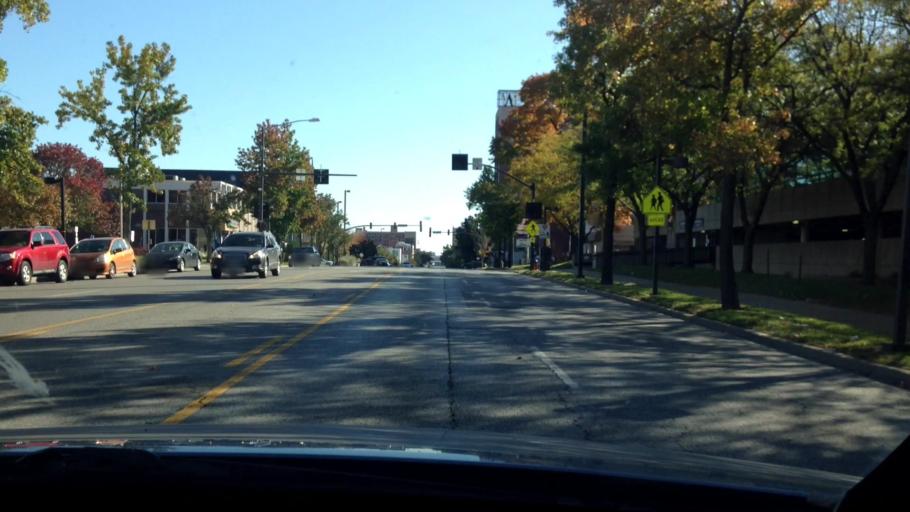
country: US
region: Missouri
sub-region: Jackson County
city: Kansas City
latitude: 39.0690
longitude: -94.5901
